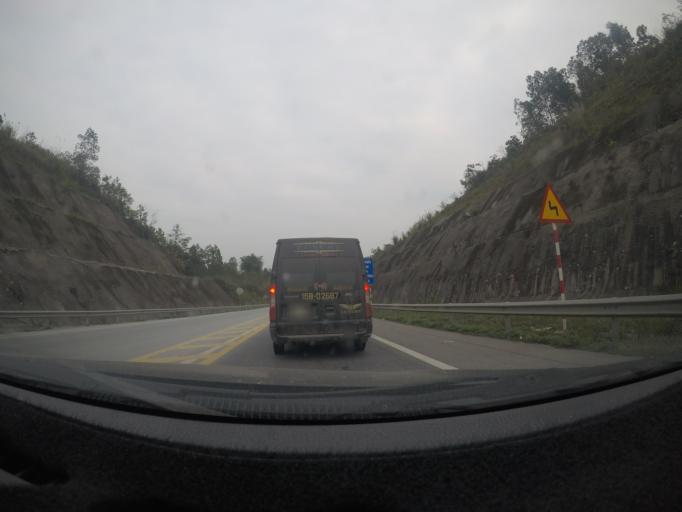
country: VN
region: Yen Bai
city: Co Phuc
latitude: 21.7921
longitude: 104.7643
